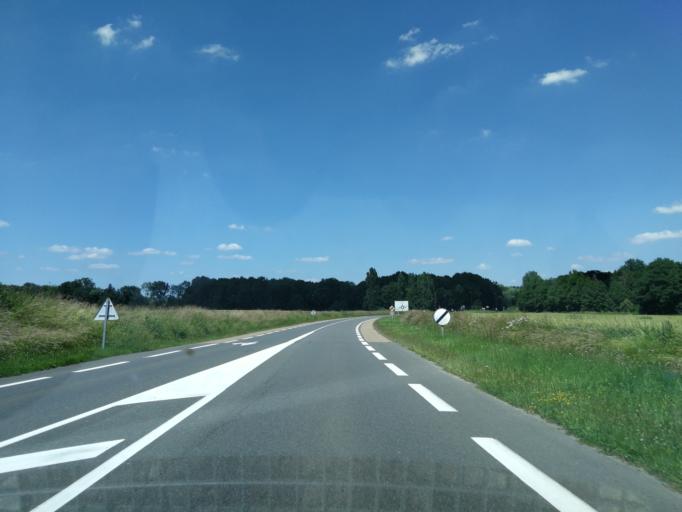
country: FR
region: Ile-de-France
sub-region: Departement de l'Essonne
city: Briis-sous-Forges
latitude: 48.6217
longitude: 2.1169
